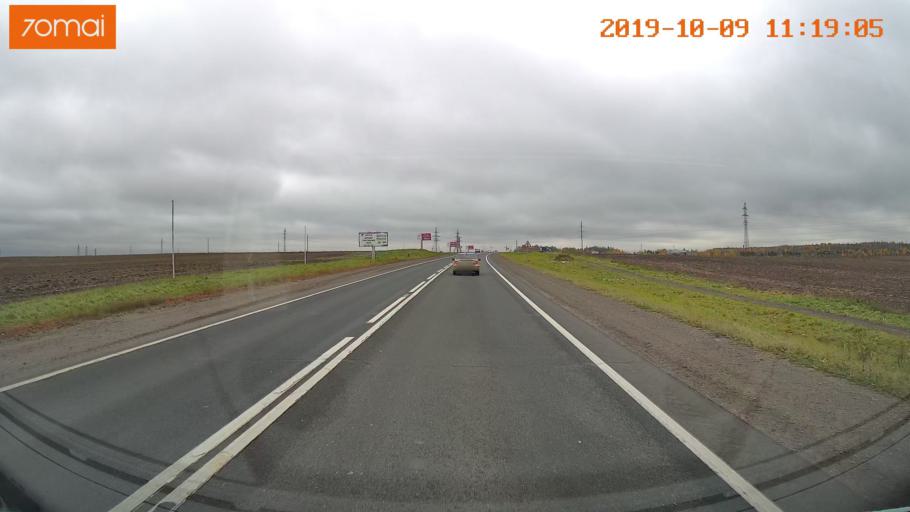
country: RU
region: Vologda
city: Vologda
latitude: 59.1626
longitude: 39.9232
